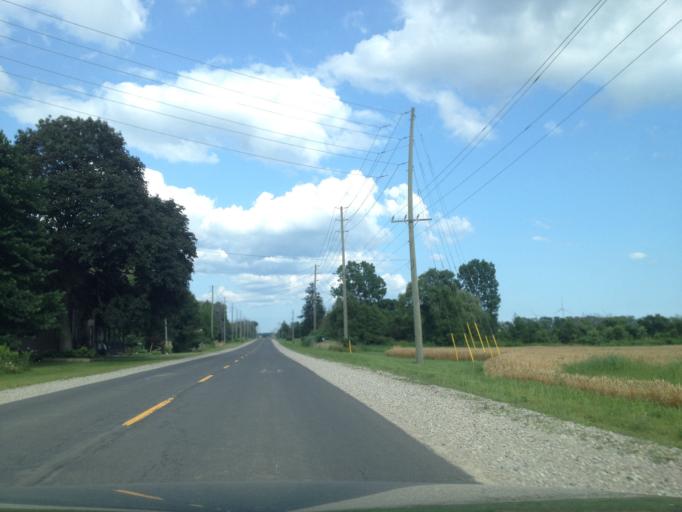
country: CA
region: Ontario
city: Aylmer
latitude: 42.6739
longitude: -80.8714
